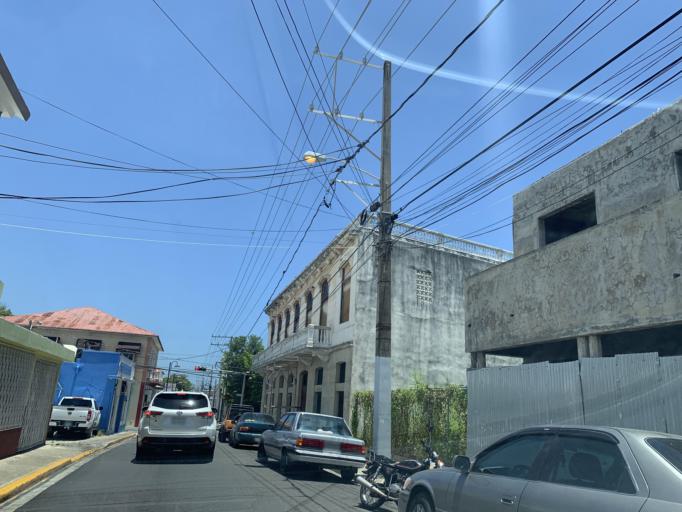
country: DO
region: Puerto Plata
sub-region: Puerto Plata
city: Puerto Plata
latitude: 19.7984
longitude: -70.6918
